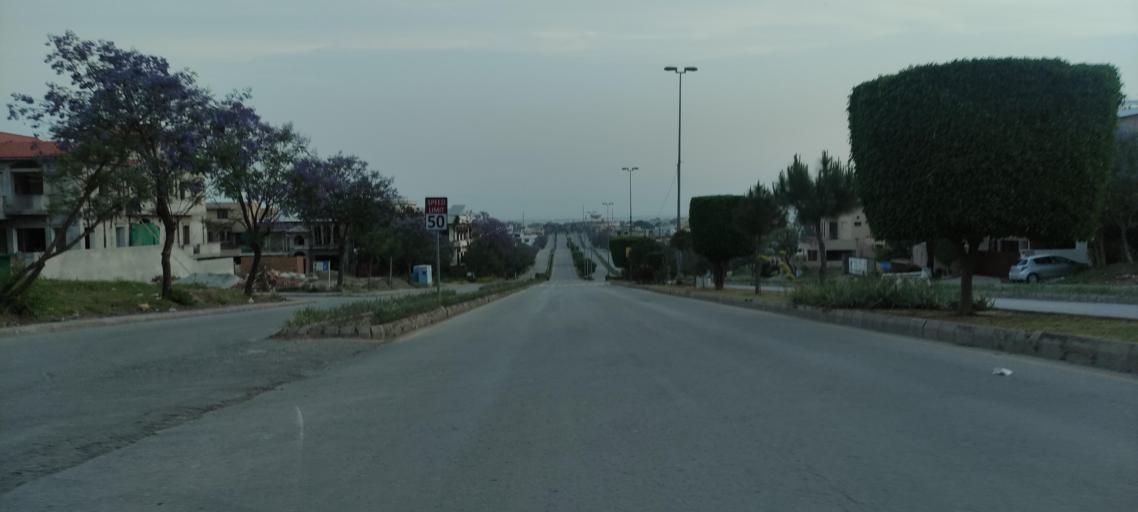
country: PK
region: Punjab
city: Rawalpindi
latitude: 33.5216
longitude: 73.1651
